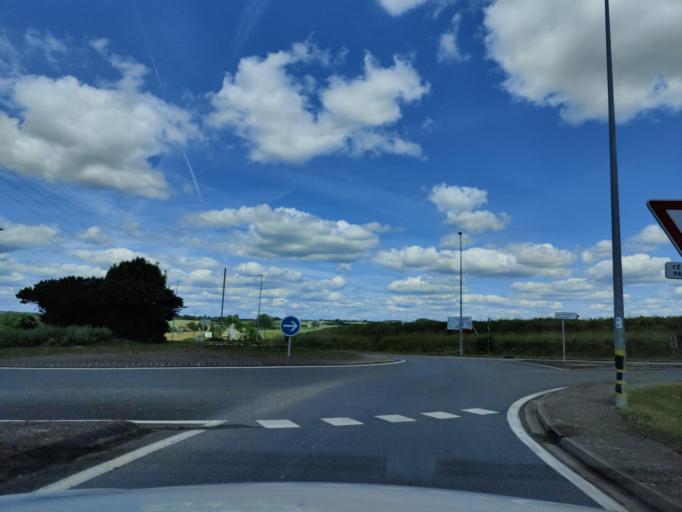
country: FR
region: Centre
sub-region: Departement du Cher
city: Fussy
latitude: 47.1509
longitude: 2.4285
